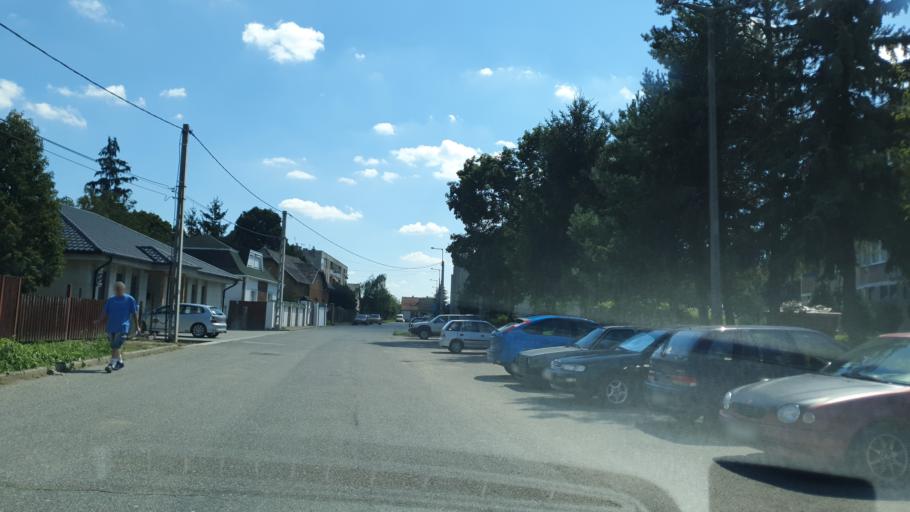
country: HU
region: Nograd
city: Szecseny
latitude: 48.0799
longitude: 19.5226
